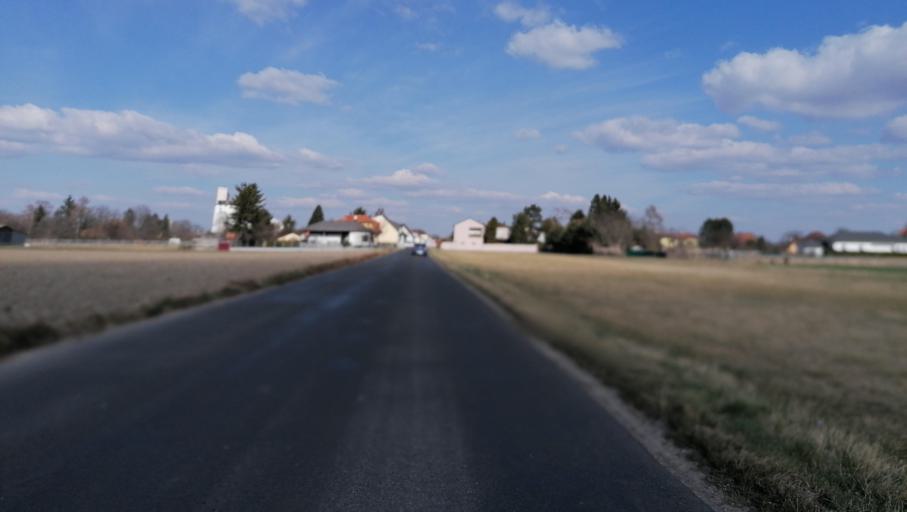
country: AT
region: Lower Austria
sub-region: Politischer Bezirk Wiener Neustadt
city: Lichtenworth
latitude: 47.8309
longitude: 16.2865
